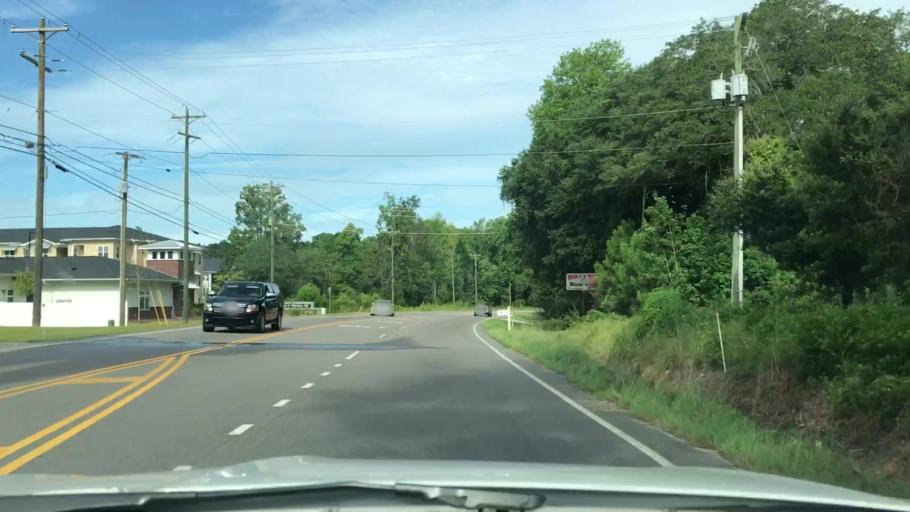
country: US
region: South Carolina
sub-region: Charleston County
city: Lincolnville
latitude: 33.0191
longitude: -80.1560
